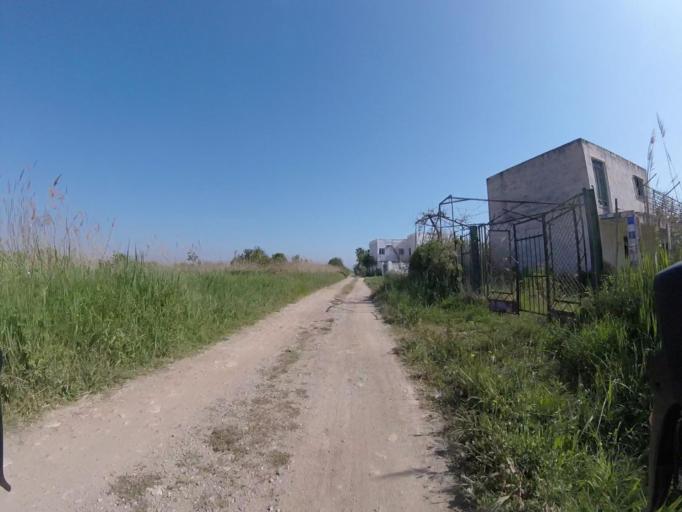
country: ES
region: Valencia
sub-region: Provincia de Castello
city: Orpesa/Oropesa del Mar
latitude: 40.1524
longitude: 0.1686
